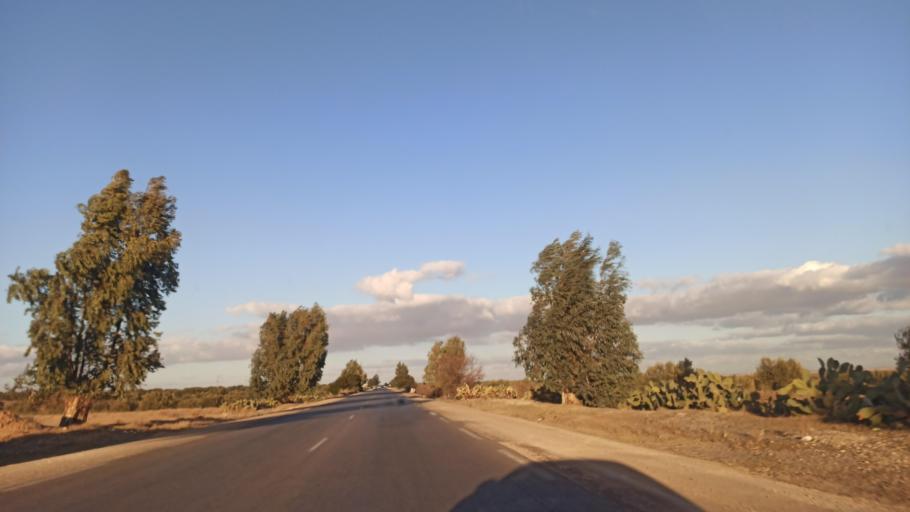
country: TN
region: Al Qayrawan
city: Sbikha
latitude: 35.8679
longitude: 10.2137
